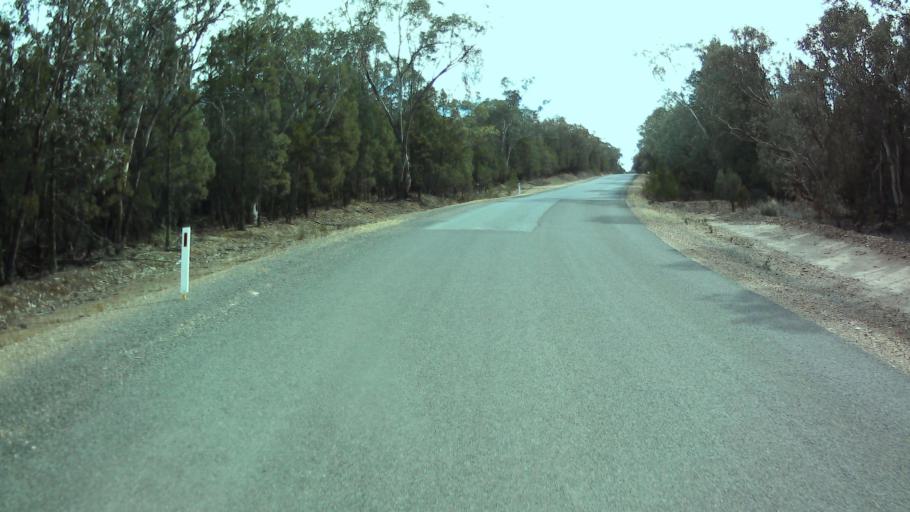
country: AU
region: New South Wales
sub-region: Weddin
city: Grenfell
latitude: -33.8959
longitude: 148.1858
